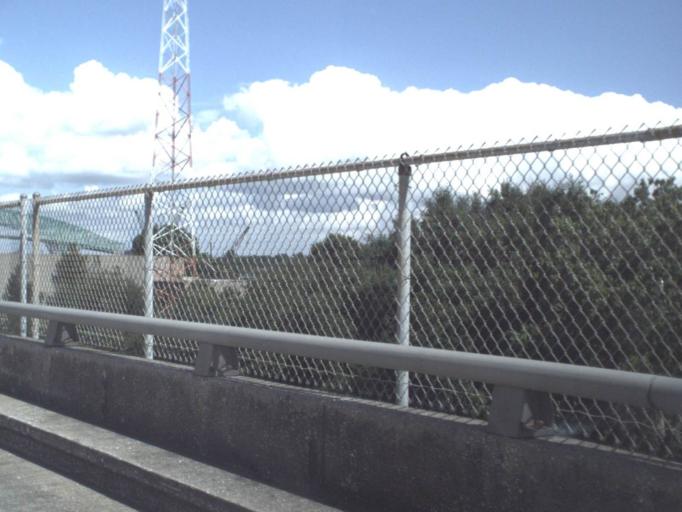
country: US
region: Florida
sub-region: Duval County
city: Jacksonville
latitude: 30.3210
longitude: -81.6385
